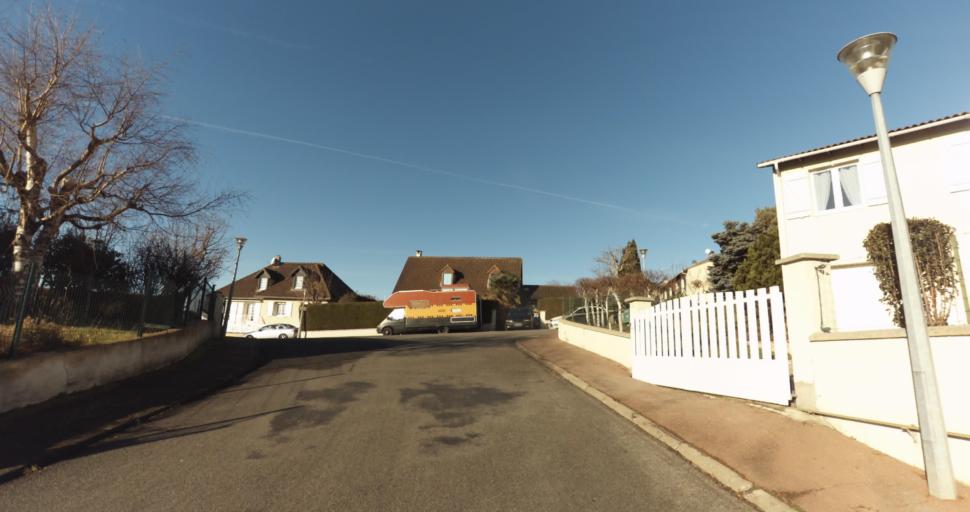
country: FR
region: Limousin
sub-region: Departement de la Haute-Vienne
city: Aixe-sur-Vienne
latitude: 45.8038
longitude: 1.1575
